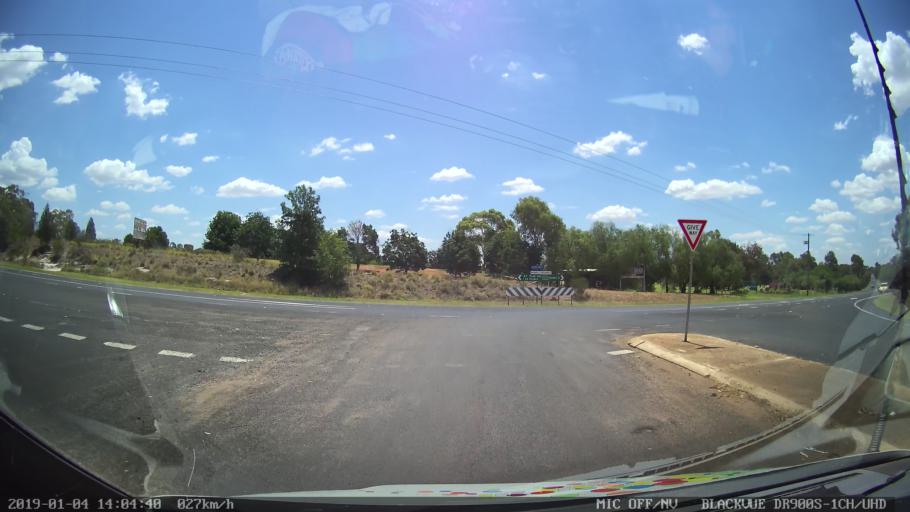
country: AU
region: New South Wales
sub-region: Dubbo Municipality
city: Dubbo
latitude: -32.2677
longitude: 148.5849
